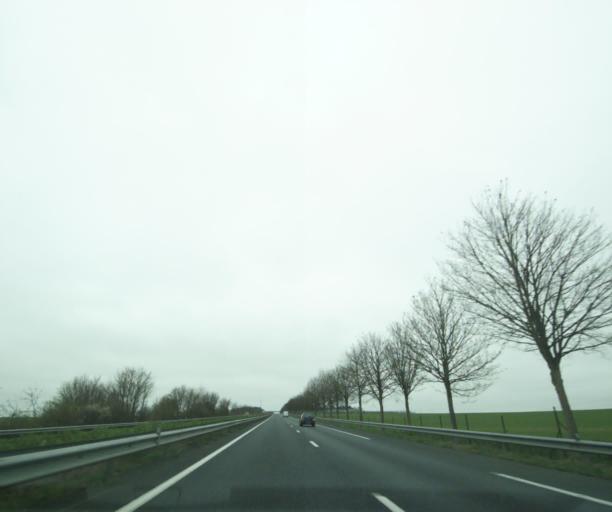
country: FR
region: Centre
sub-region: Departement de l'Indre
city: Vatan
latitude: 47.0016
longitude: 1.7776
